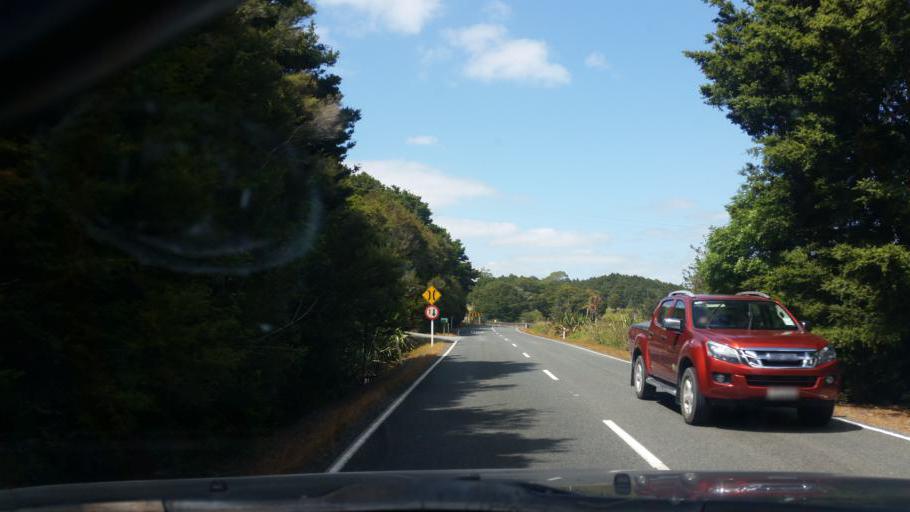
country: NZ
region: Northland
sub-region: Whangarei
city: Ruakaka
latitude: -35.9750
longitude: 174.2885
